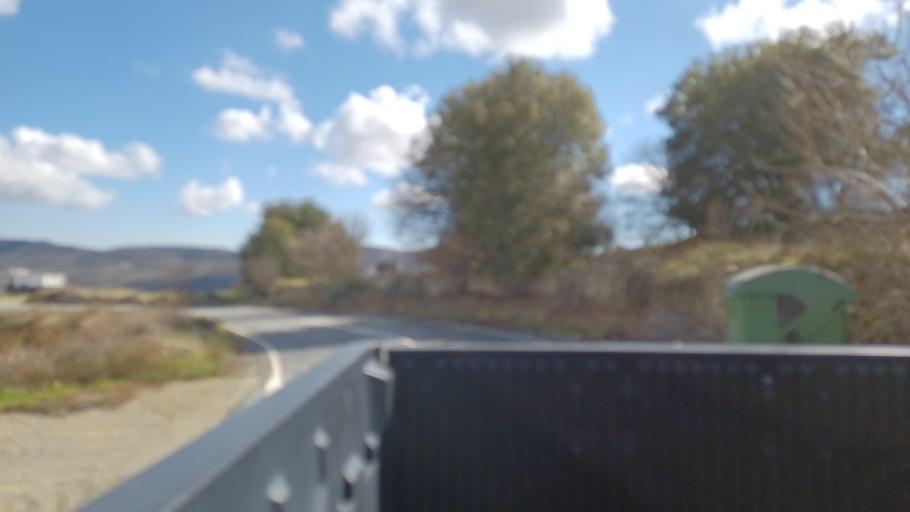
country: CY
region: Limassol
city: Pachna
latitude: 34.7862
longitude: 32.7380
